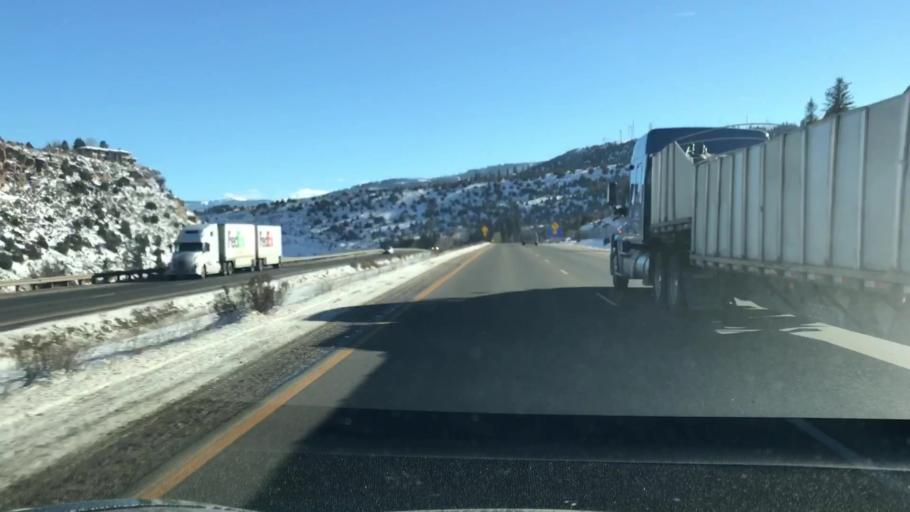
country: US
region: Colorado
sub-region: Eagle County
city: Edwards
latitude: 39.7070
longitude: -106.6918
